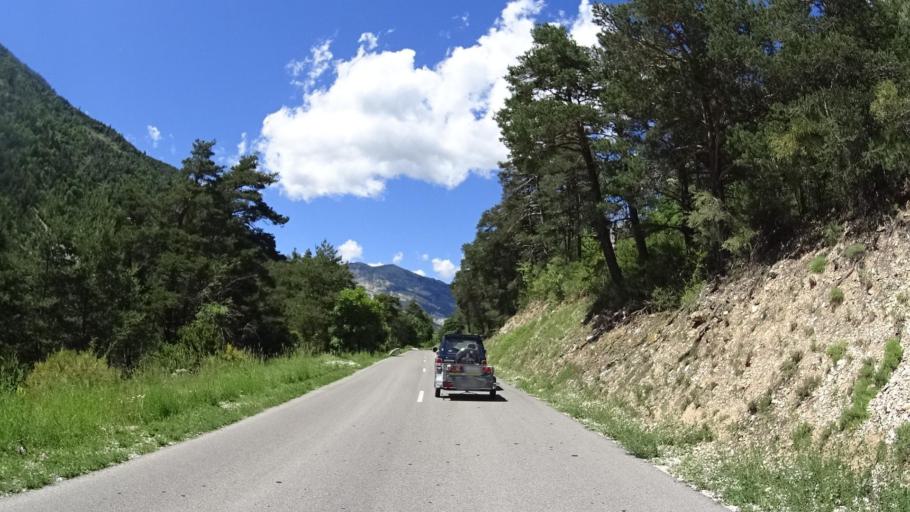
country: FR
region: Provence-Alpes-Cote d'Azur
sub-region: Departement des Alpes-de-Haute-Provence
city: Annot
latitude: 44.0669
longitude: 6.5748
